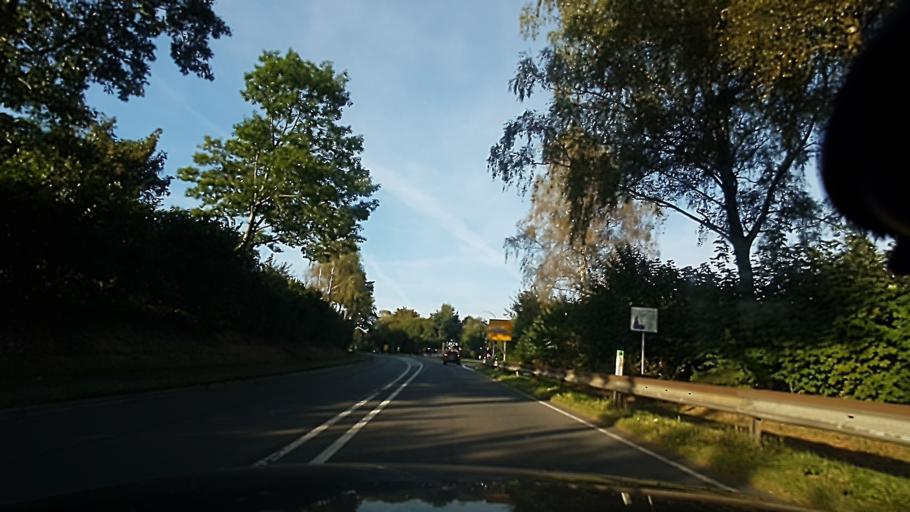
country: DE
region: North Rhine-Westphalia
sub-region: Regierungsbezirk Koln
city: Marienheide
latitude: 51.0644
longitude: 7.5580
